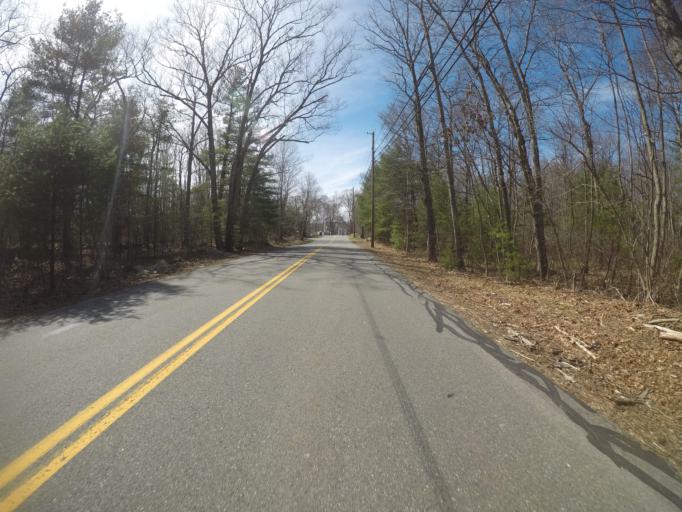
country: US
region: Massachusetts
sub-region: Bristol County
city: Easton
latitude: 42.0355
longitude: -71.0925
